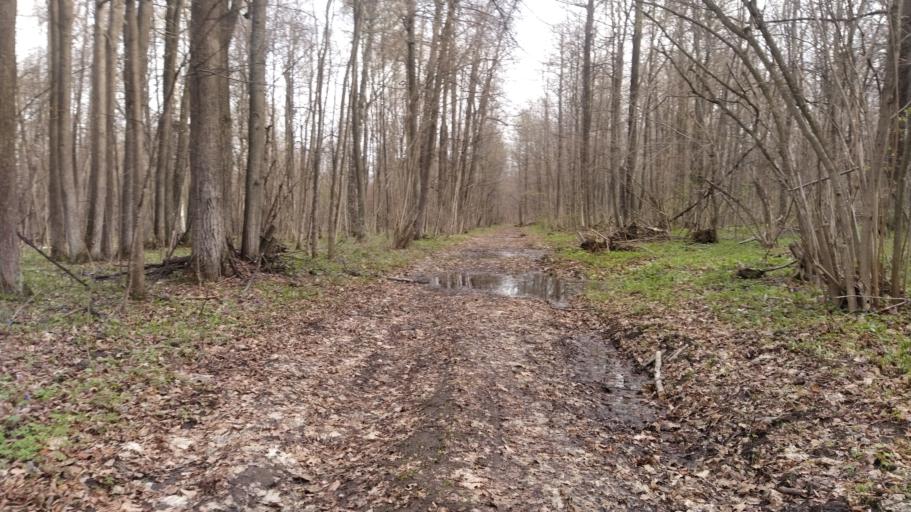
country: RU
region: Chuvashia
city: Novyye Lapsary
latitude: 56.1348
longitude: 47.1210
